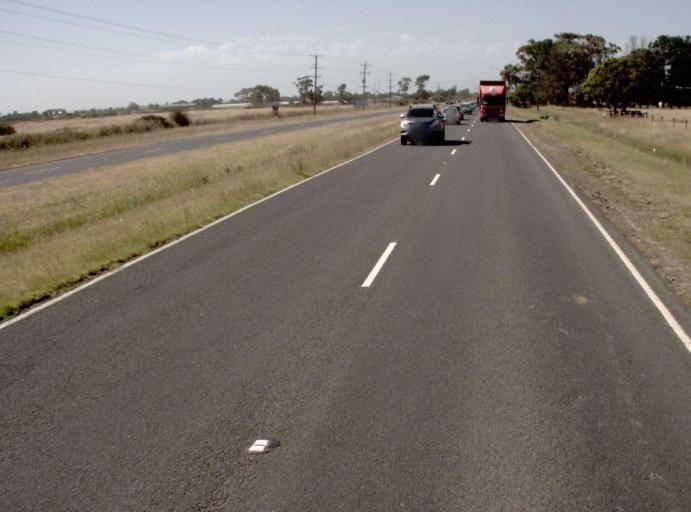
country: AU
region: Victoria
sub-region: Frankston
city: Sandhurst
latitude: -38.0557
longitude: 145.2073
